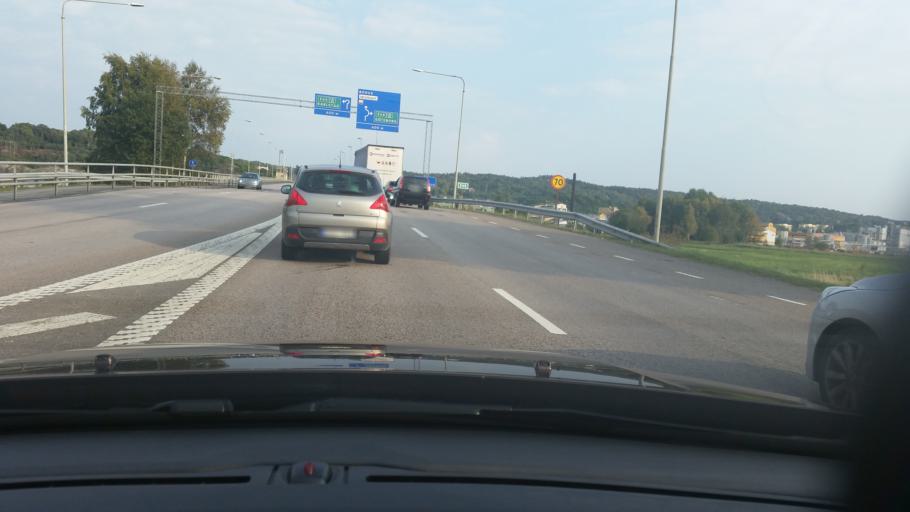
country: SE
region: Vaestra Goetaland
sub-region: Kungalvs Kommun
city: Kungalv
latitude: 57.8567
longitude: 12.0034
